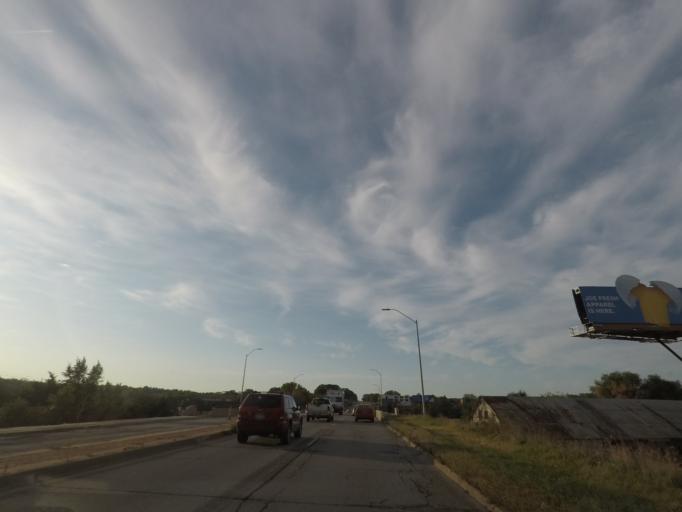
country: US
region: Iowa
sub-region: Polk County
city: Des Moines
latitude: 41.5668
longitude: -93.6450
